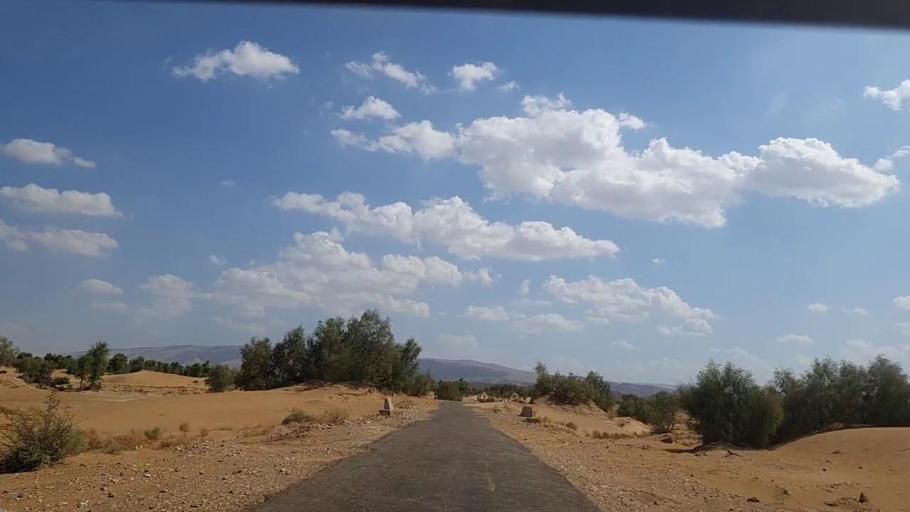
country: PK
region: Sindh
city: Johi
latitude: 26.5128
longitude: 67.4481
